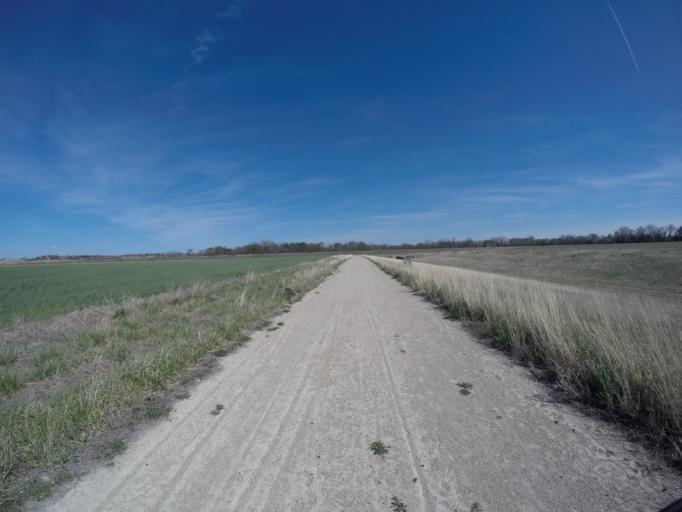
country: US
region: Kansas
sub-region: Saline County
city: Salina
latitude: 38.7791
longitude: -97.5816
